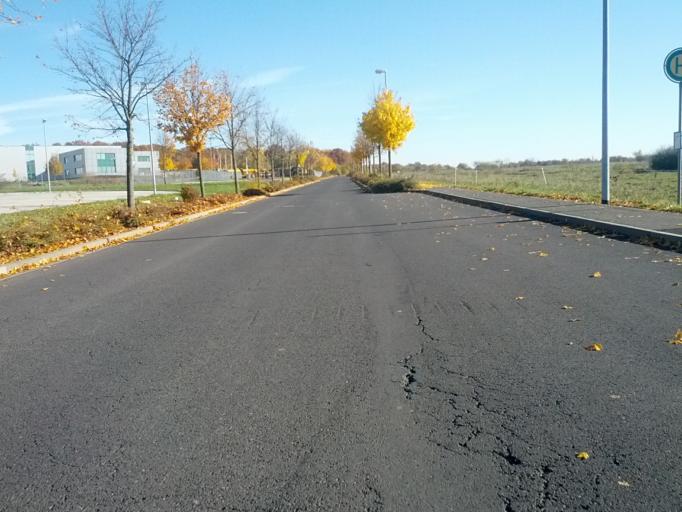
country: DE
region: Thuringia
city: Haina
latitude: 50.9988
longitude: 10.4553
